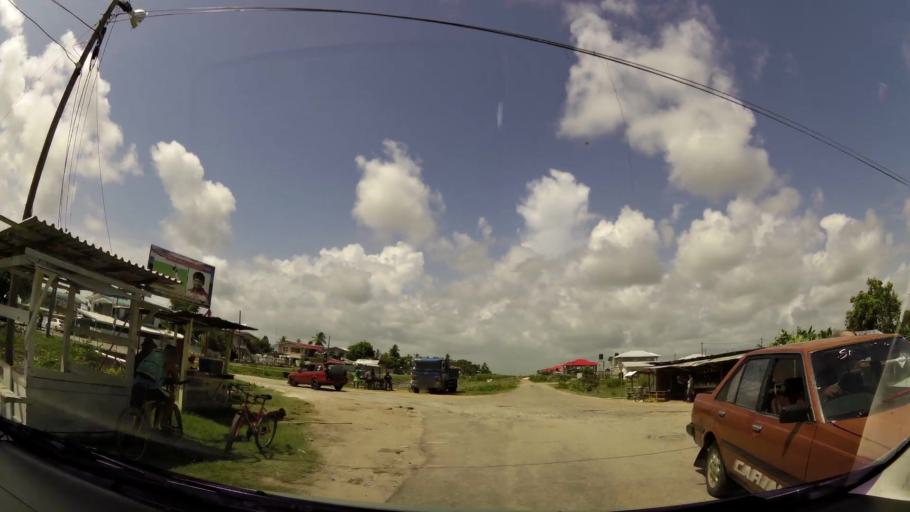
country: GY
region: Demerara-Mahaica
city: Mahaica Village
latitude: 6.7683
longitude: -58.0114
